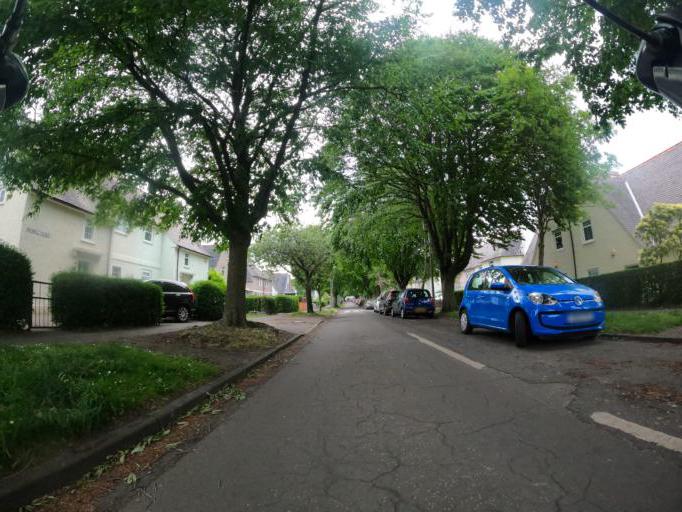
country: GB
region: Scotland
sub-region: Edinburgh
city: Edinburgh
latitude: 55.9722
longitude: -3.2212
